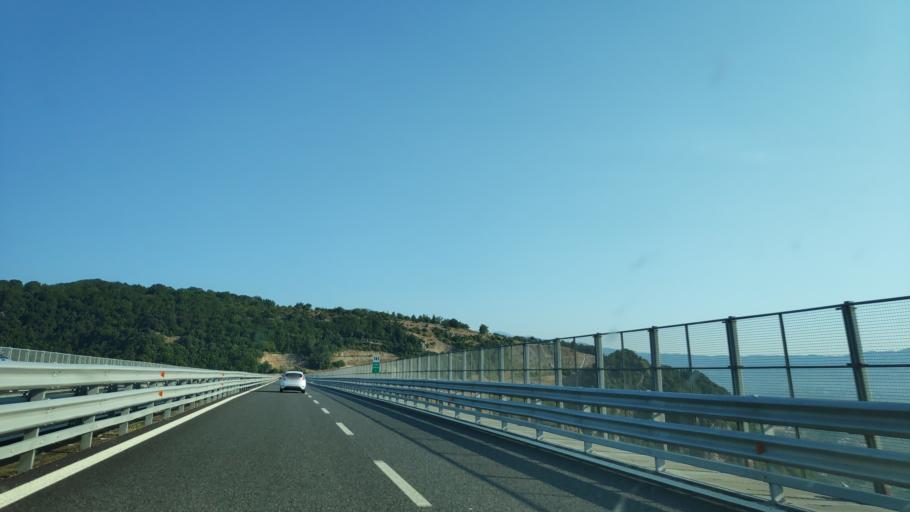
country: IT
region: Calabria
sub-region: Provincia di Cosenza
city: Laino Castello-Nuovo Centro
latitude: 39.9377
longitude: 15.9599
